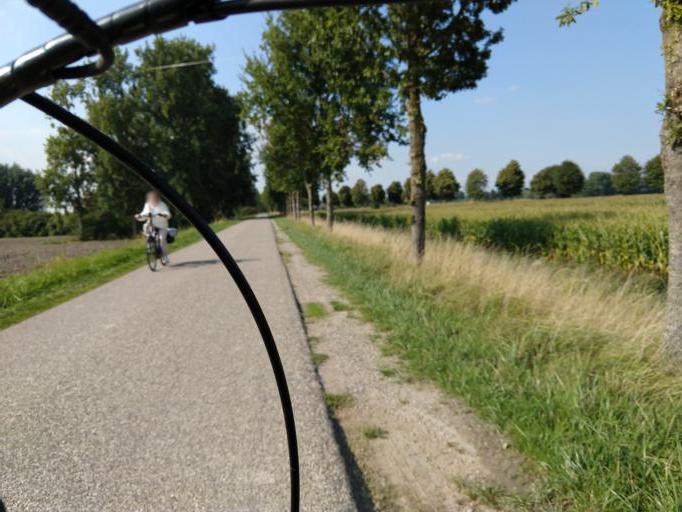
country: NL
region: Zeeland
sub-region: Gemeente Goes
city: Goes
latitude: 51.4332
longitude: 3.8399
